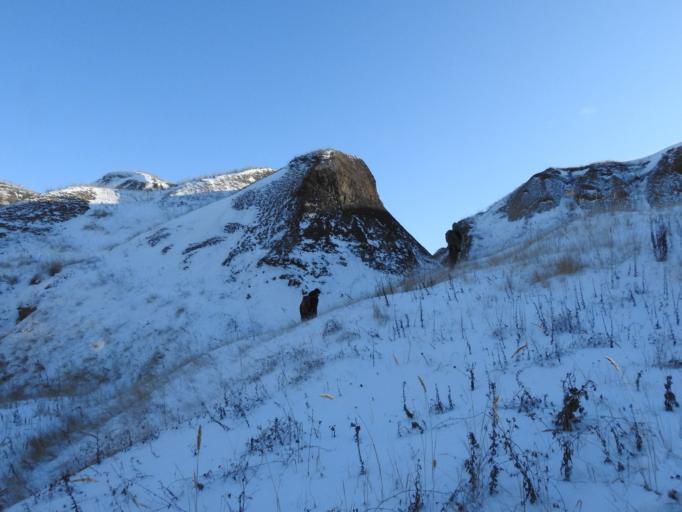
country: RU
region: Saratov
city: Lysyye Gory
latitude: 51.4584
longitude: 44.9683
